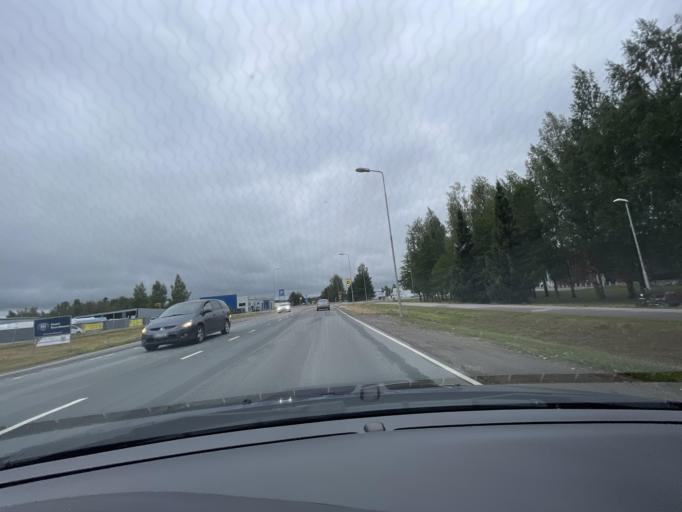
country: FI
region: Haeme
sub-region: Riihimaeki
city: Riihimaeki
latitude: 60.7237
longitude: 24.7507
